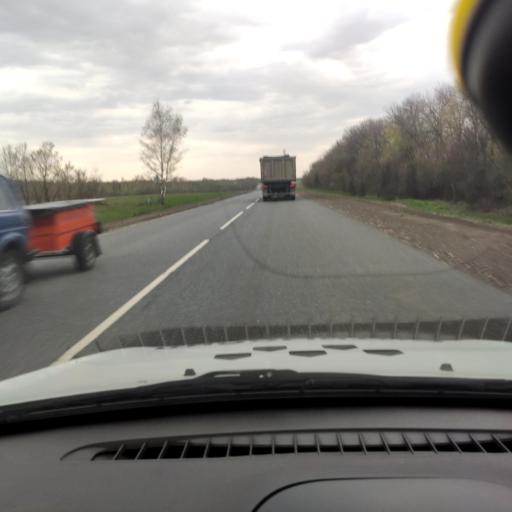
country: RU
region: Samara
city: Zhigulevsk
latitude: 53.2887
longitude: 49.3272
